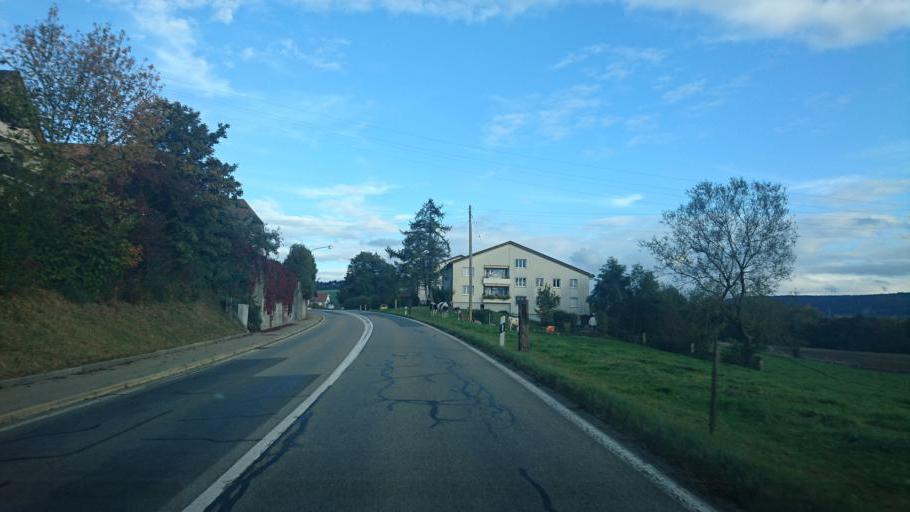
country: CH
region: Bern
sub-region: Bern-Mittelland District
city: Worb
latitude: 46.9285
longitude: 7.5798
